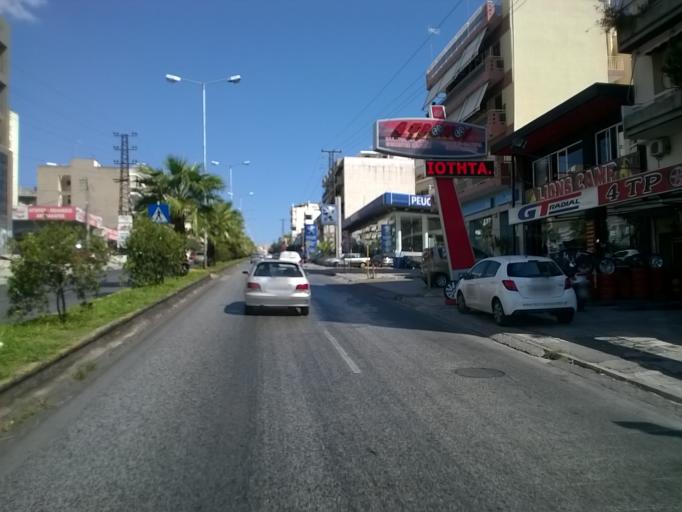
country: GR
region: Attica
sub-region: Nomos Piraios
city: Keratsini
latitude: 37.9722
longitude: 23.6225
